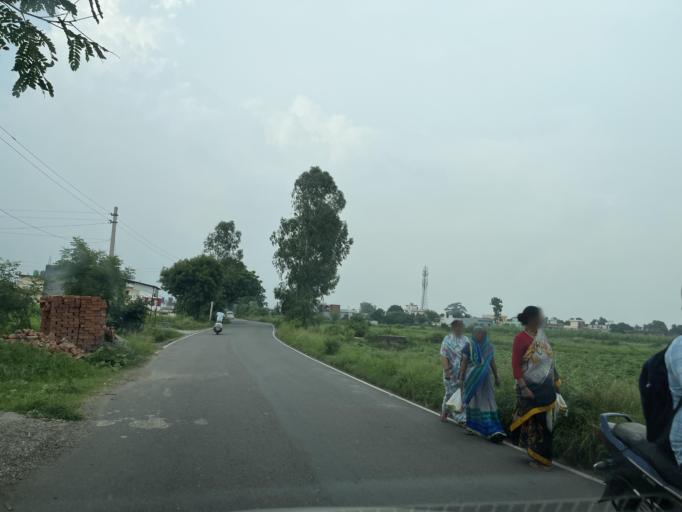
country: IN
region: Uttarakhand
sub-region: Naini Tal
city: Haldwani
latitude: 29.1777
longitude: 79.4718
